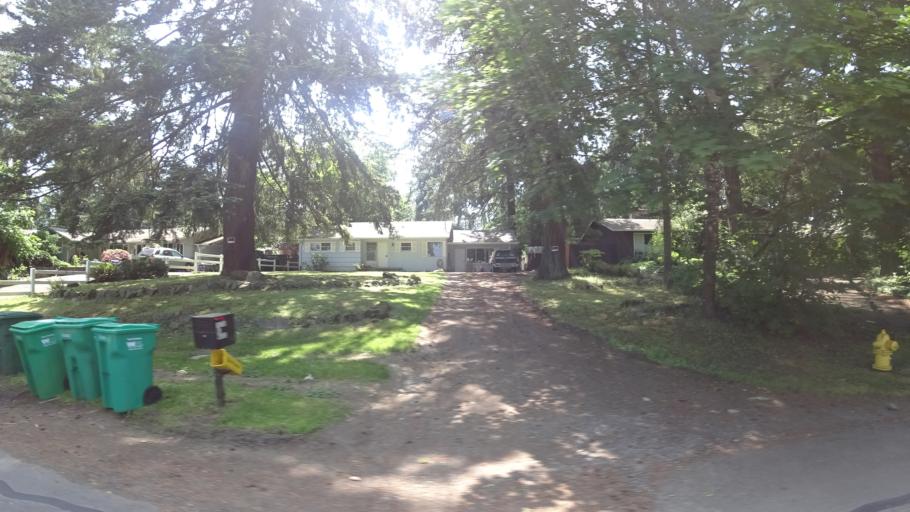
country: US
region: Oregon
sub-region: Multnomah County
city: Fairview
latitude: 45.5322
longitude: -122.4906
